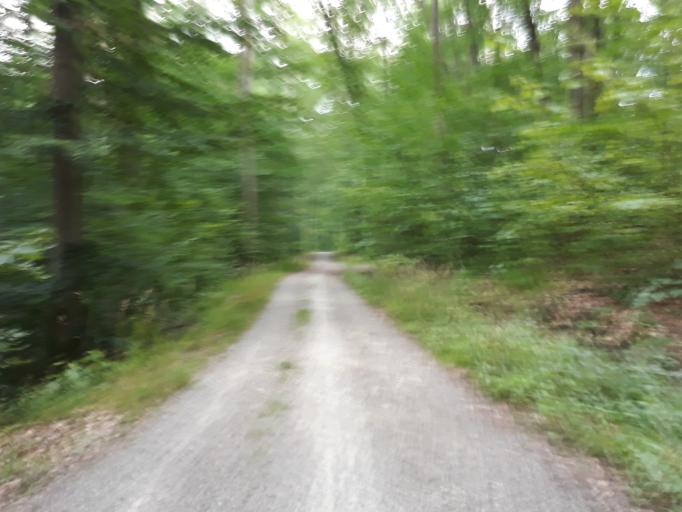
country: DE
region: Baden-Wuerttemberg
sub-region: Regierungsbezirk Stuttgart
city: Schonaich
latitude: 48.6700
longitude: 9.0553
